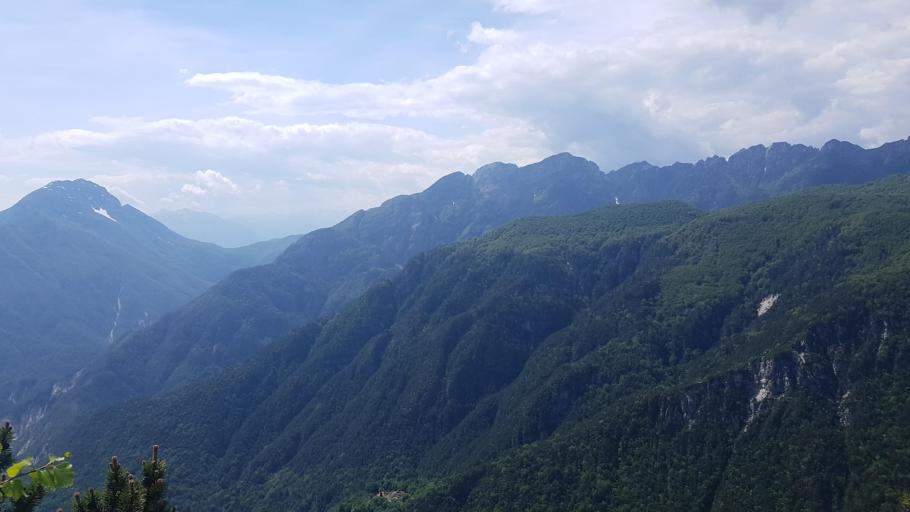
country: IT
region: Friuli Venezia Giulia
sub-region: Provincia di Udine
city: Moggio Udinese
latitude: 46.4343
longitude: 13.1819
